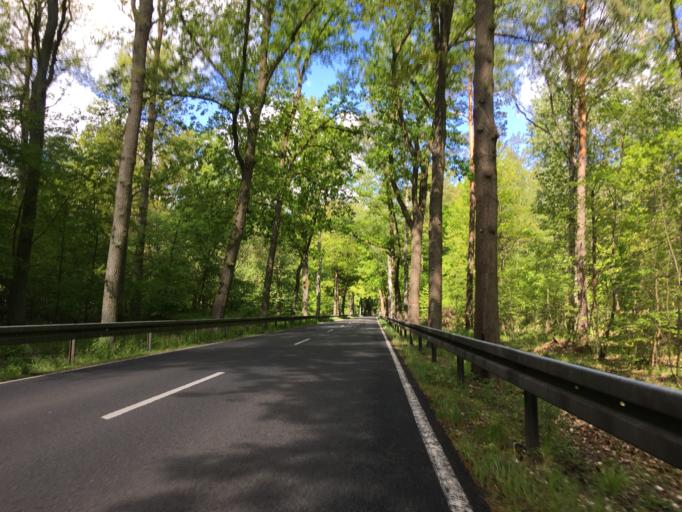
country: DE
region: Brandenburg
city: Oranienburg
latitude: 52.7355
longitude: 13.2890
